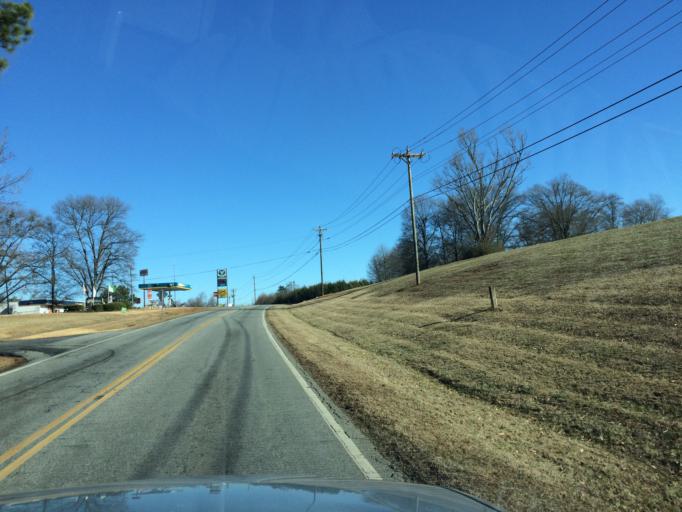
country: US
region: South Carolina
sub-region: Spartanburg County
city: Fairforest
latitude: 34.9638
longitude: -82.0022
